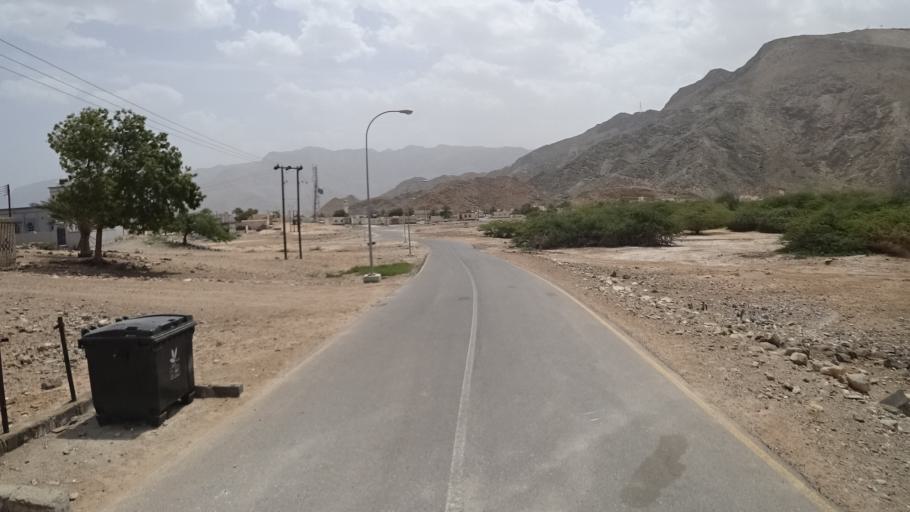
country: OM
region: Muhafazat Masqat
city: Muscat
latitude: 23.4354
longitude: 58.7809
